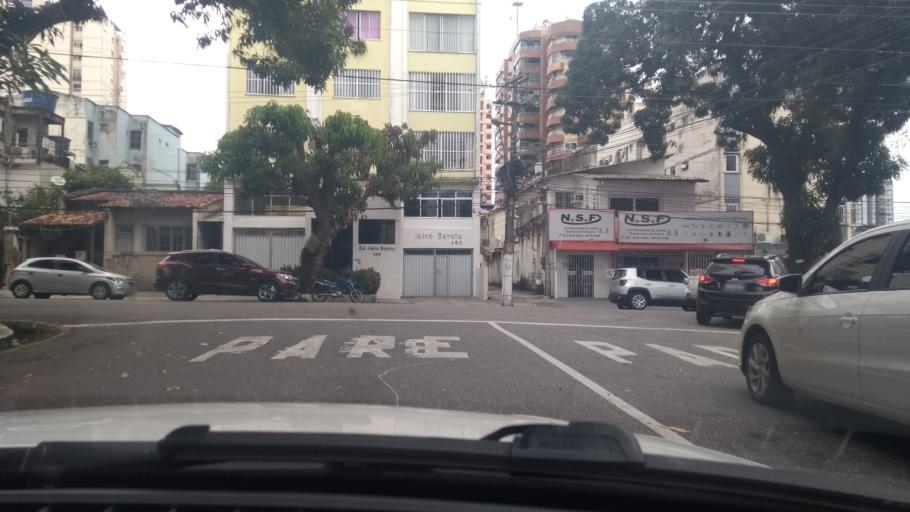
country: BR
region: Para
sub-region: Belem
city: Belem
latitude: -1.4608
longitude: -48.4933
